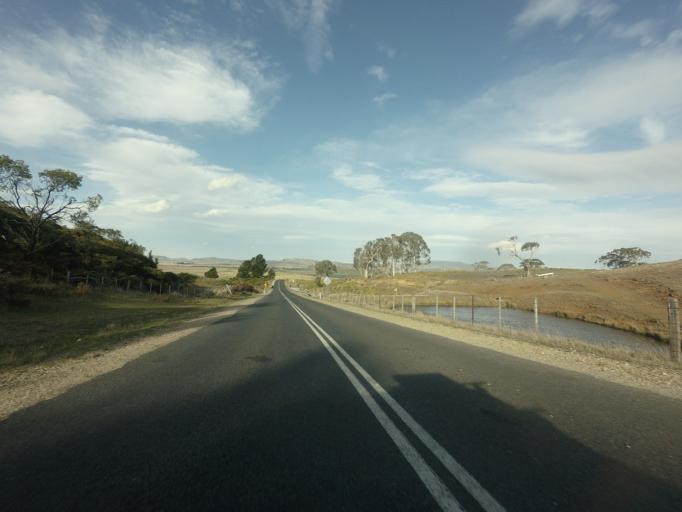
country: AU
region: Tasmania
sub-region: Derwent Valley
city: New Norfolk
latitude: -42.3468
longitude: 146.9837
